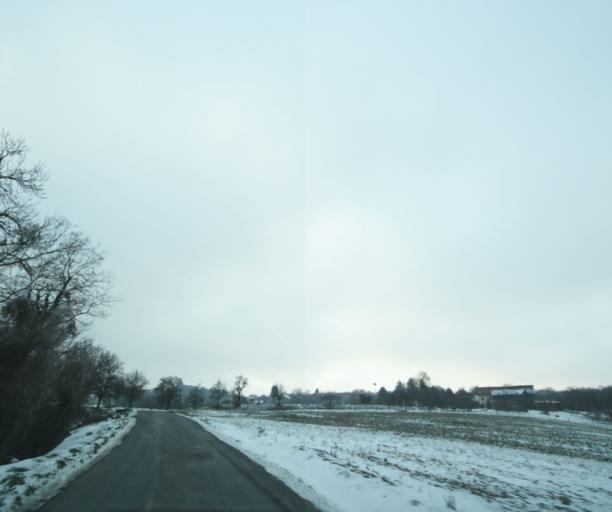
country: FR
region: Rhone-Alpes
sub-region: Departement de la Haute-Savoie
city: Reignier-Esery
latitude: 46.1261
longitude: 6.2594
